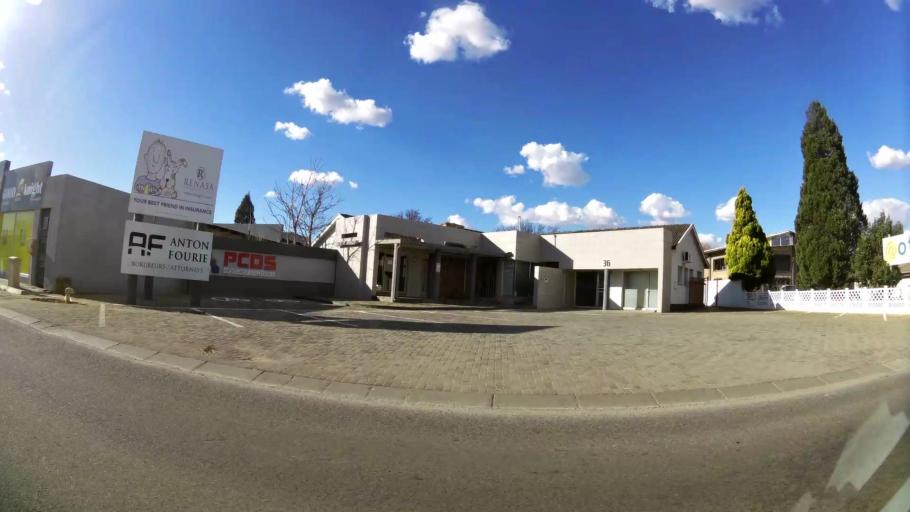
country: ZA
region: North-West
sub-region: Dr Kenneth Kaunda District Municipality
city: Klerksdorp
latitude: -26.8496
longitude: 26.6759
